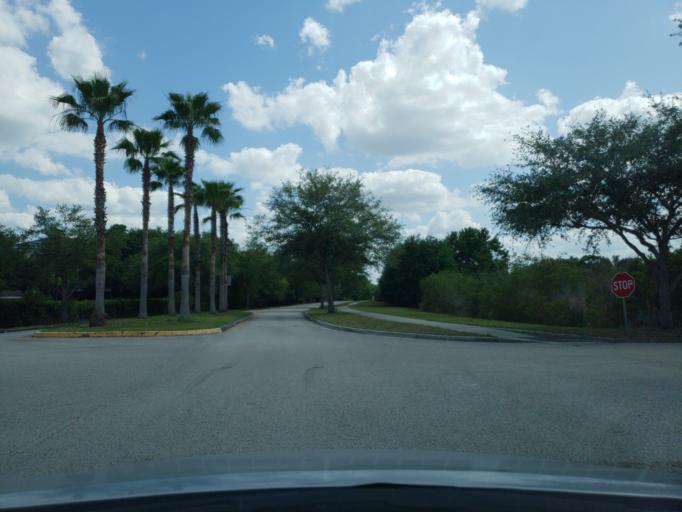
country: US
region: Florida
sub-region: Hillsborough County
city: Progress Village
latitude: 27.9221
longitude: -82.3445
